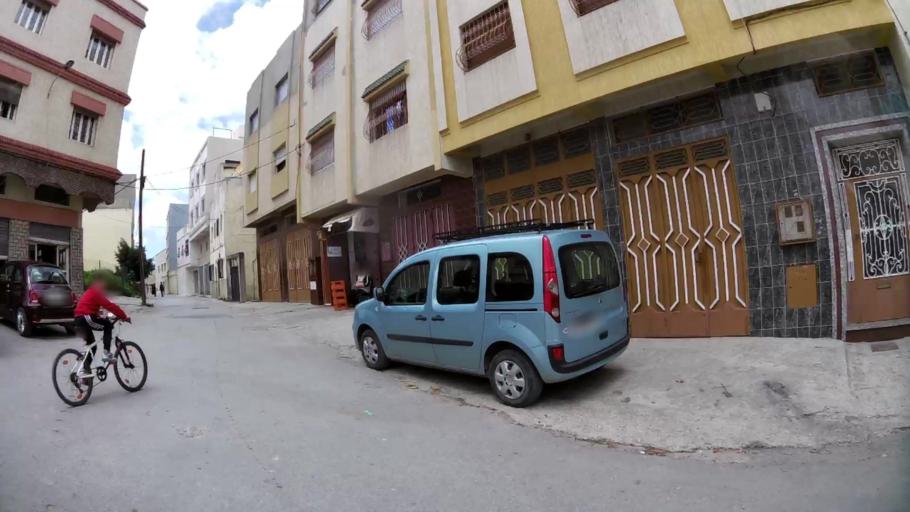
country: MA
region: Tanger-Tetouan
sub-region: Tanger-Assilah
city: Tangier
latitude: 35.7706
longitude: -5.7718
